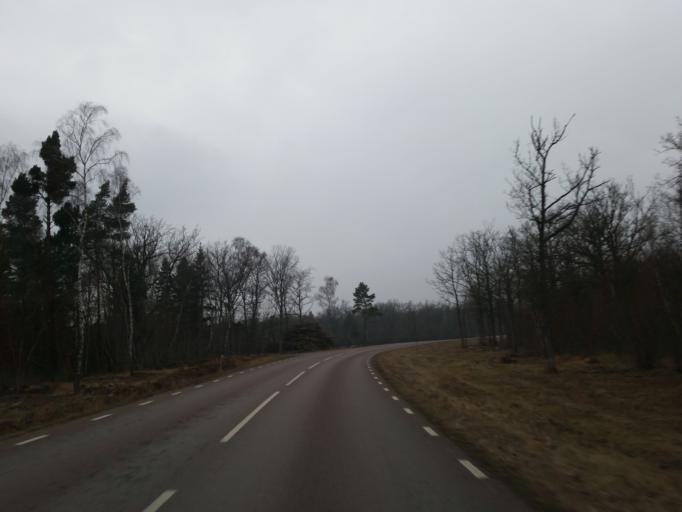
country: SE
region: Kalmar
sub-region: Morbylanga Kommun
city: Sodra Sandby
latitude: 56.6378
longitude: 16.5827
